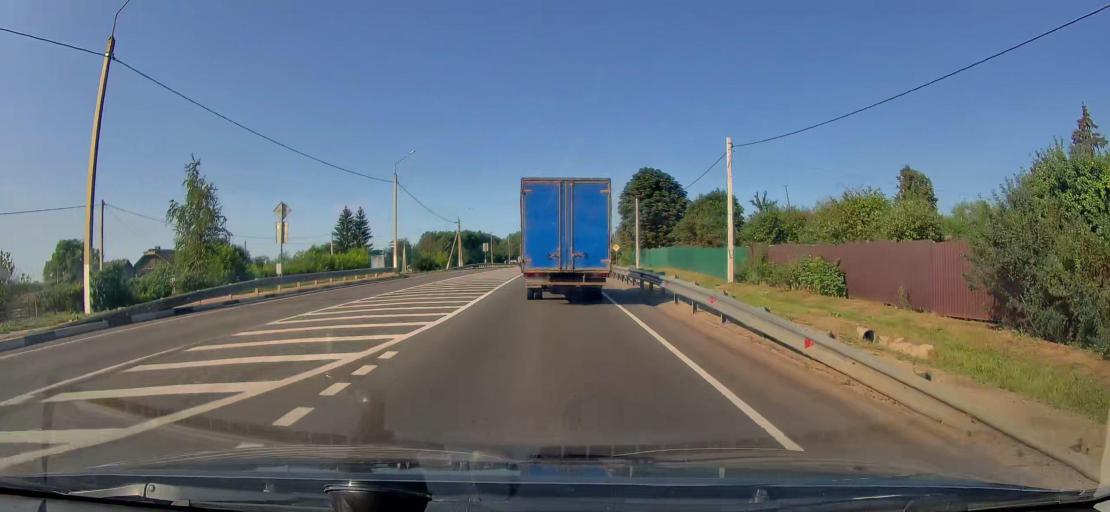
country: RU
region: Orjol
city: Mtsensk
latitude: 53.1532
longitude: 36.3681
